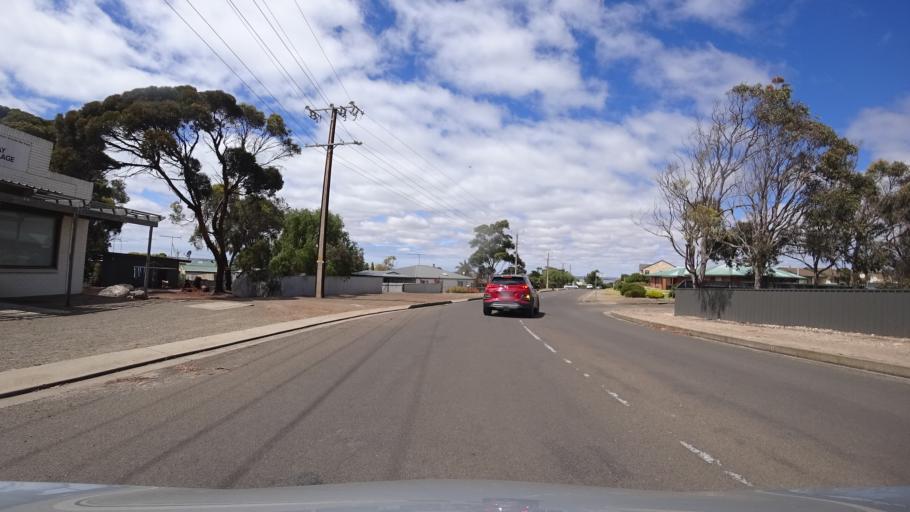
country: AU
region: South Australia
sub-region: Kangaroo Island
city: Kingscote
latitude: -35.6579
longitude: 137.6337
